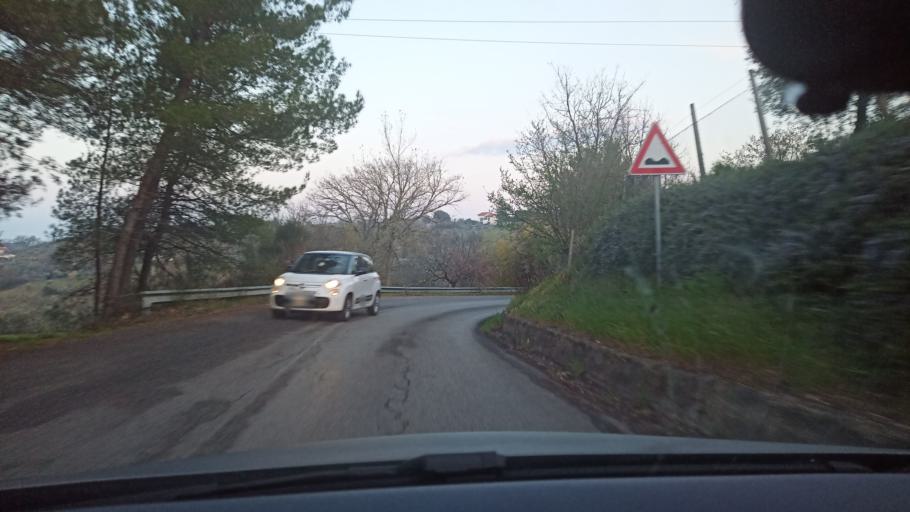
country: IT
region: Latium
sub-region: Provincia di Rieti
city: Vacone
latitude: 42.3644
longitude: 12.6614
